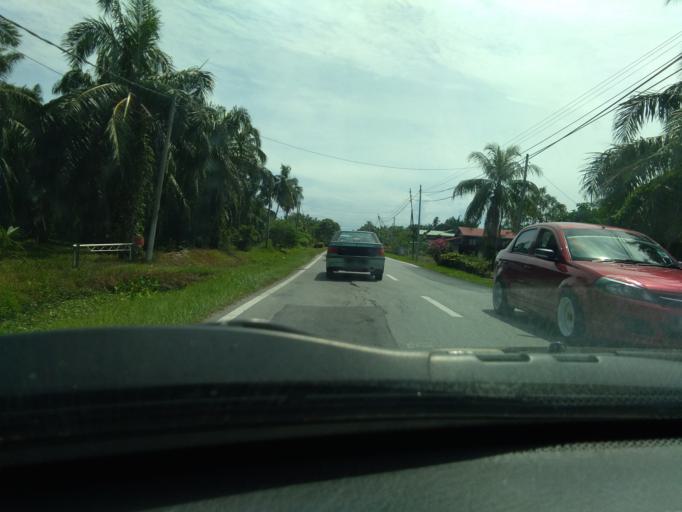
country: MY
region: Perak
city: Bagan Serai
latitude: 5.0286
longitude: 100.5578
